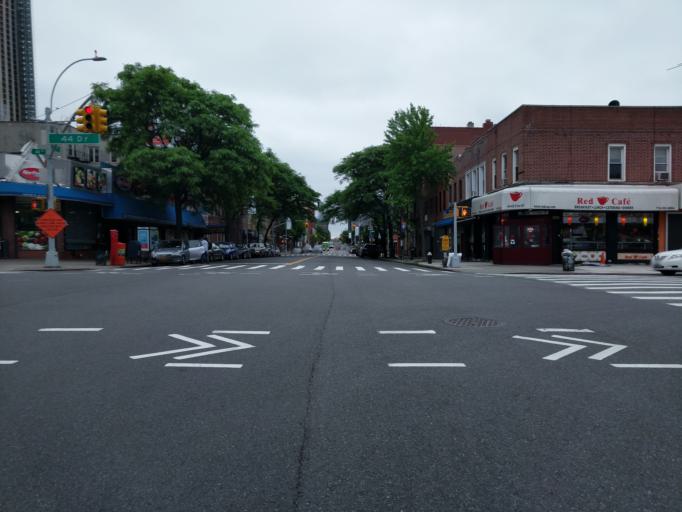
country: US
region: New York
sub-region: Queens County
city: Long Island City
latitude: 40.7482
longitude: -73.9474
